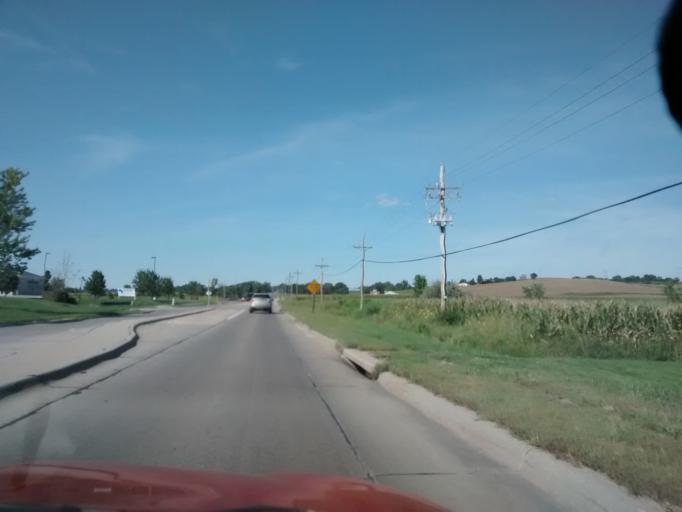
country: US
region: Nebraska
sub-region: Sarpy County
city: Offutt Air Force Base
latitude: 41.1425
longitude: -95.9667
